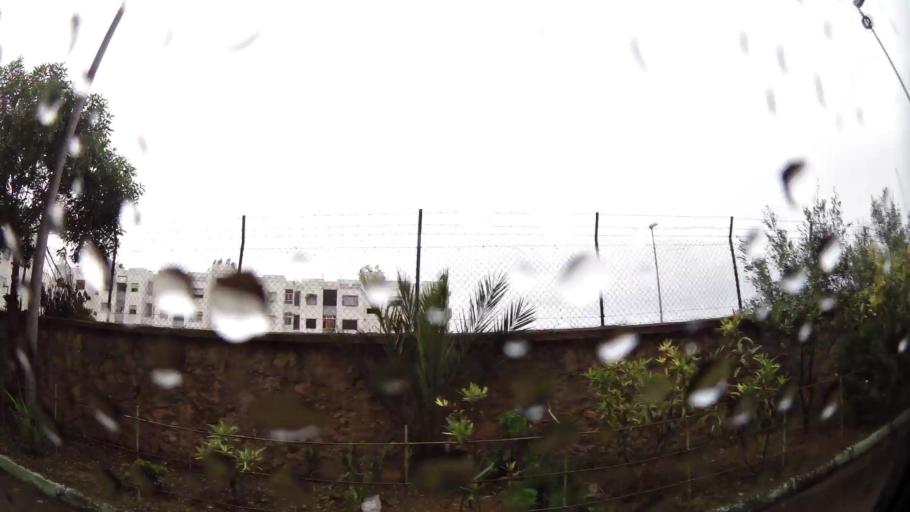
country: MA
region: Grand Casablanca
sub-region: Mediouna
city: Tit Mellil
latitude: 33.6230
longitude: -7.4840
